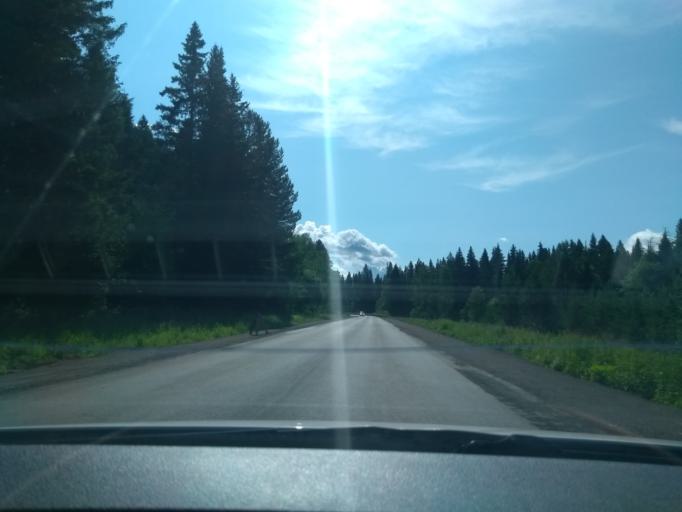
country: RU
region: Perm
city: Bershet'
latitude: 57.8186
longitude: 56.5264
